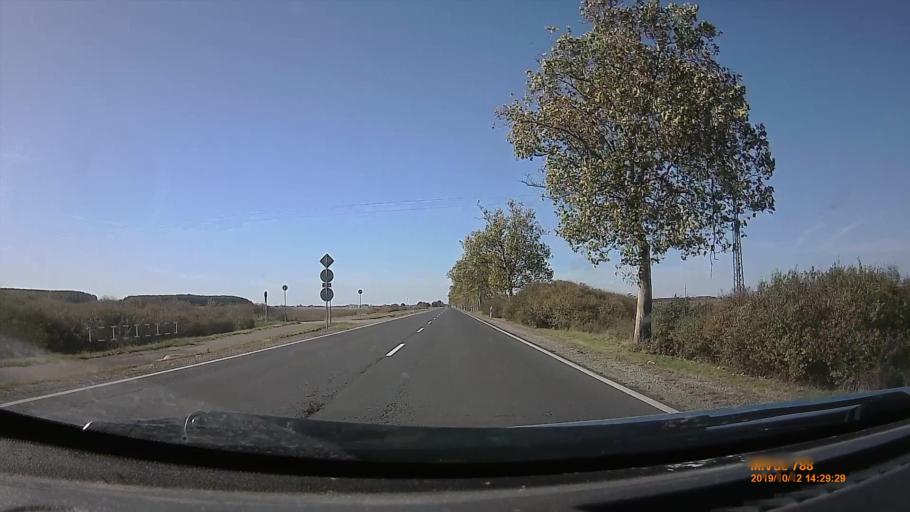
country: HU
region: Hajdu-Bihar
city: Berettyoujfalu
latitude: 47.1705
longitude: 21.6120
